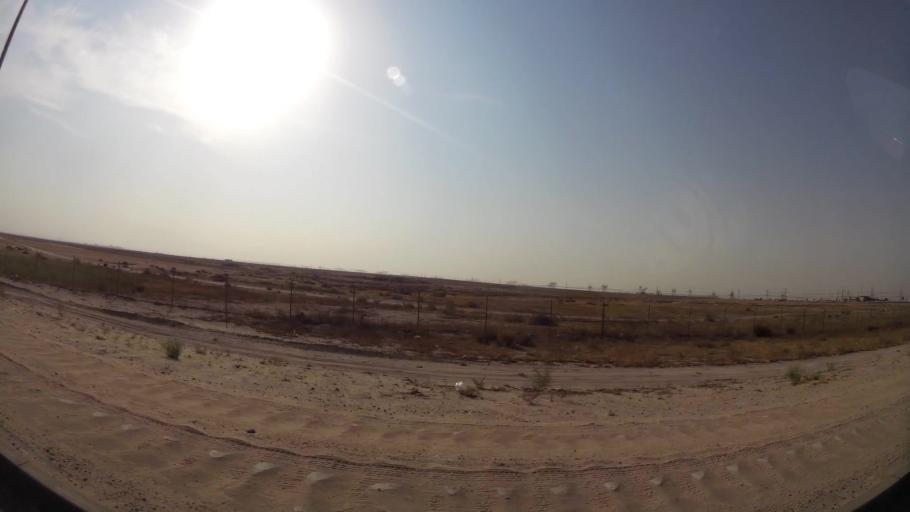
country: KW
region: Al Farwaniyah
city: Janub as Surrah
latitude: 29.1778
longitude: 47.9924
